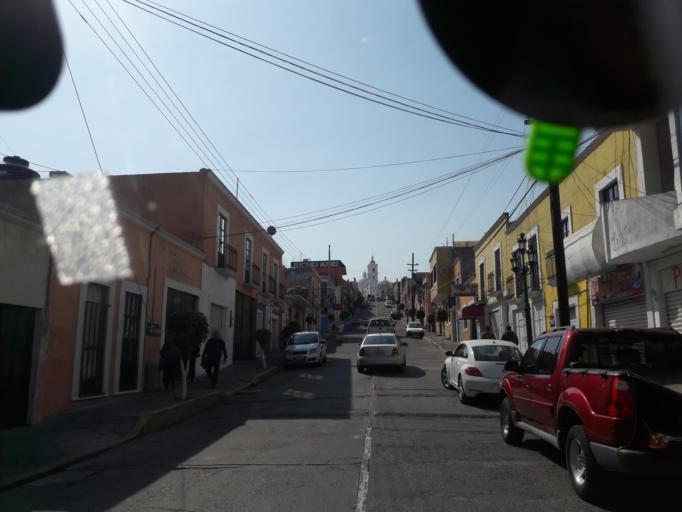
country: MX
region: Tlaxcala
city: Panotla
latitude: 19.3163
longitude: -98.2690
